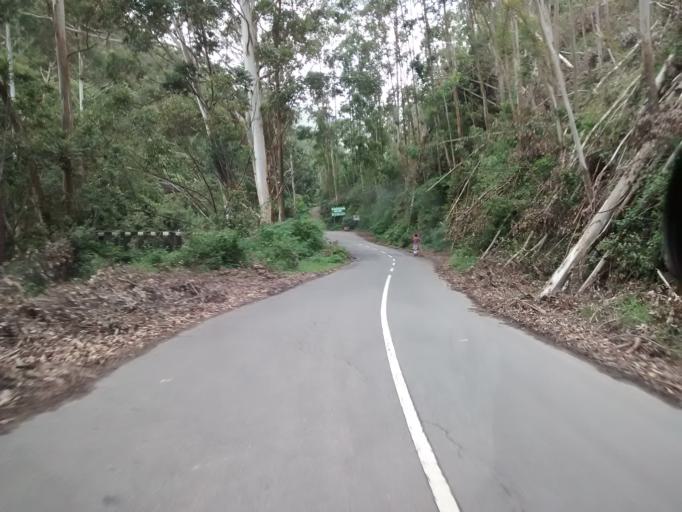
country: IN
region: Kerala
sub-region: Idukki
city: Munnar
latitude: 10.1171
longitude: 77.1496
